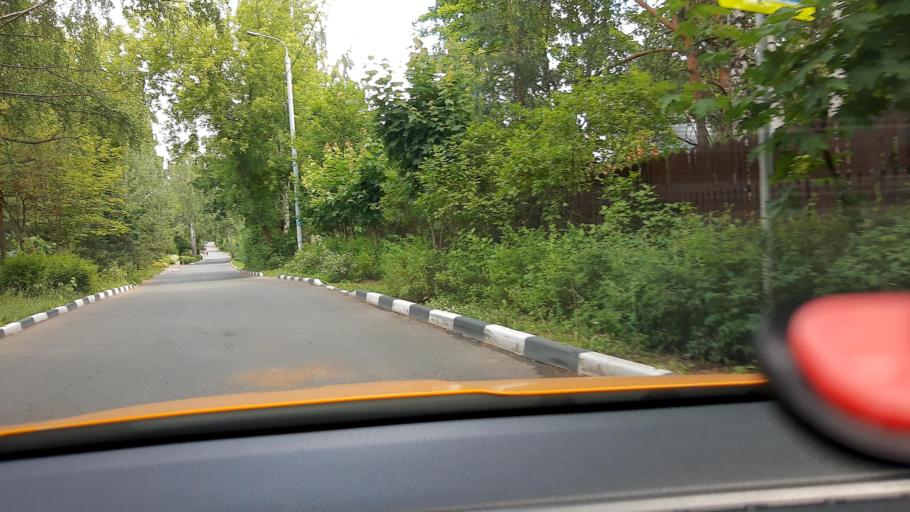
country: RU
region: Moskovskaya
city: Barvikha
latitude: 55.7385
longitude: 37.2500
